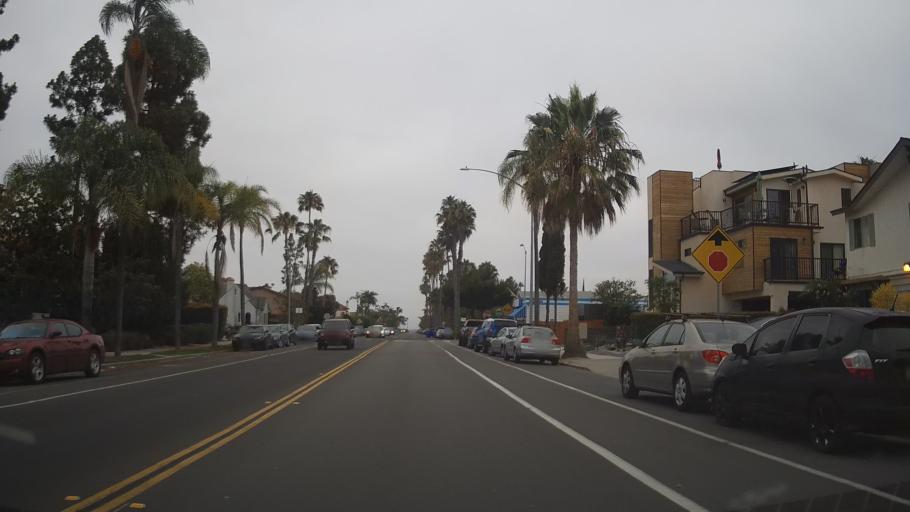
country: US
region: California
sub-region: San Diego County
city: San Diego
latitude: 32.7565
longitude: -117.1500
